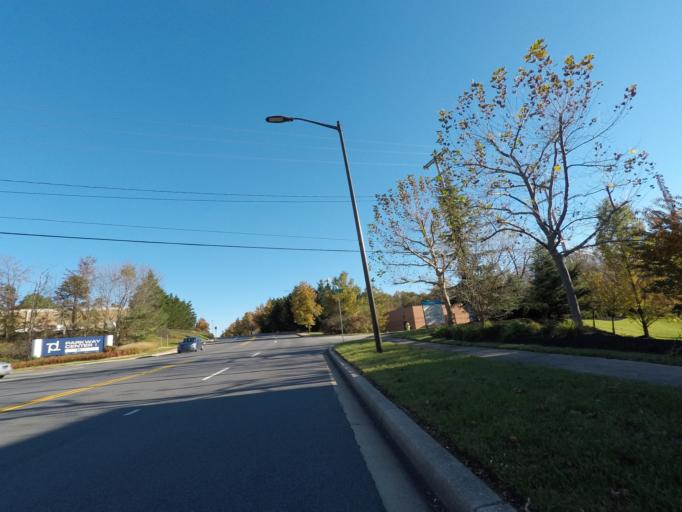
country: US
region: Maryland
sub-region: Howard County
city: Hanover
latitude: 39.1798
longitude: -76.7329
